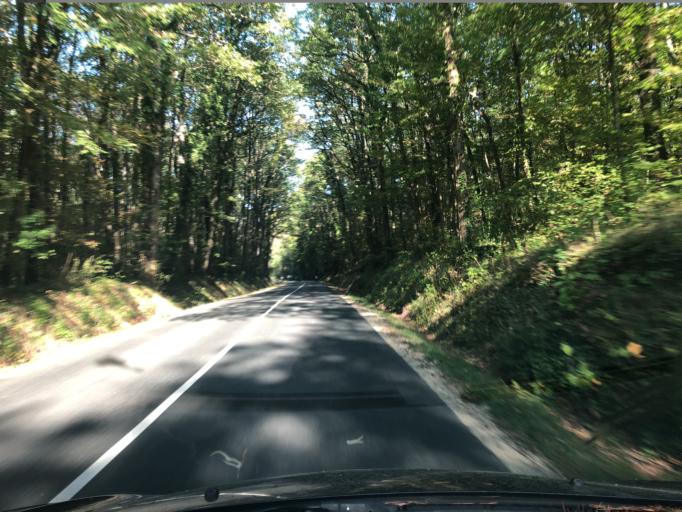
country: FR
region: Centre
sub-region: Departement d'Indre-et-Loire
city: Cerelles
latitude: 47.4791
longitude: 0.6636
